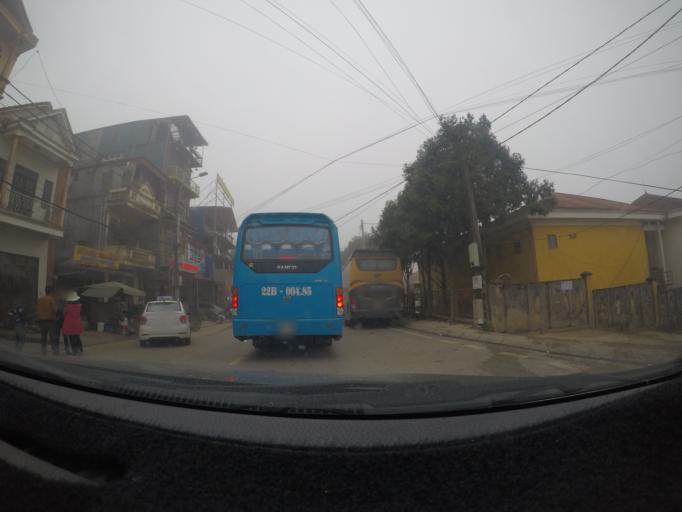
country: VN
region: Lao Cai
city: Sa Pa
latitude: 22.3401
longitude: 103.8449
